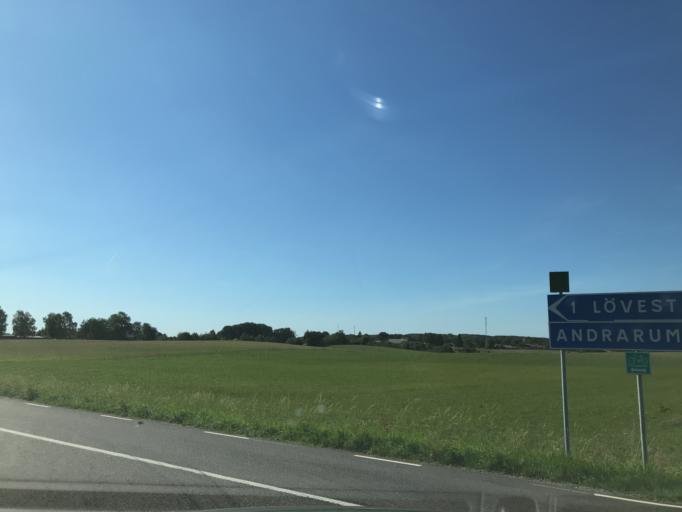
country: SE
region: Skane
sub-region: Tomelilla Kommun
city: Tomelilla
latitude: 55.6553
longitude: 13.9044
